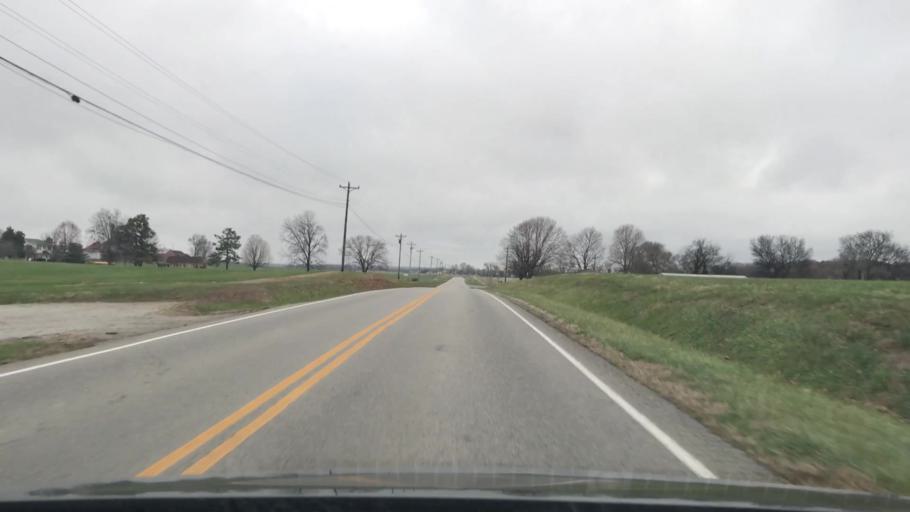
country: US
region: Kentucky
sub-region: Todd County
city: Elkton
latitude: 36.7637
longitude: -87.1671
